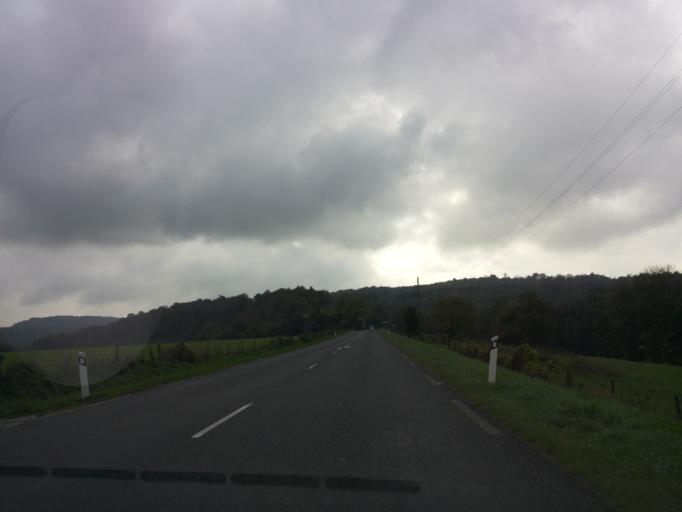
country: FR
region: Lorraine
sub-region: Departement de la Meuse
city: Montmedy
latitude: 49.5006
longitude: 5.3882
